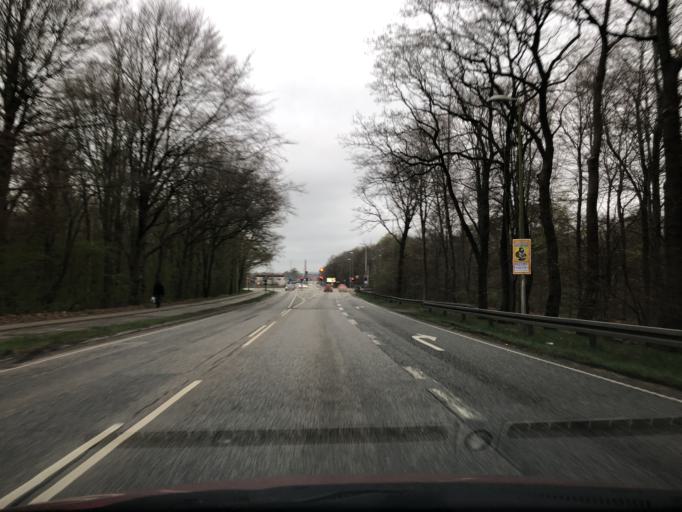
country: DK
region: Central Jutland
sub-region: Holstebro Kommune
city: Holstebro
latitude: 56.3447
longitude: 8.6332
